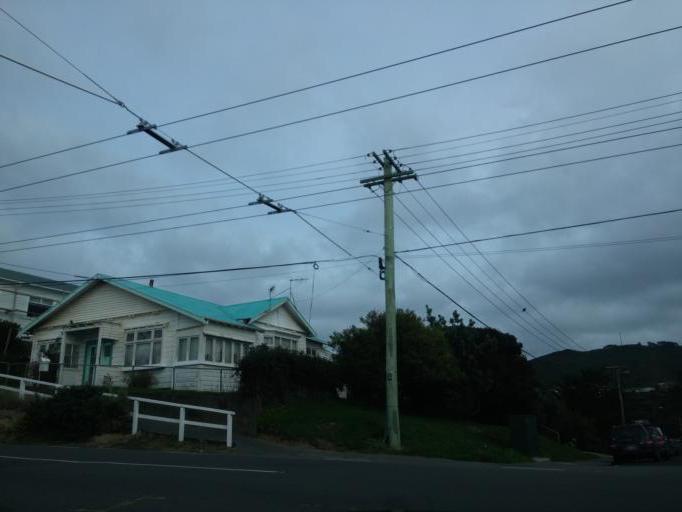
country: NZ
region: Wellington
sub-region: Wellington City
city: Brooklyn
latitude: -41.3124
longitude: 174.7660
